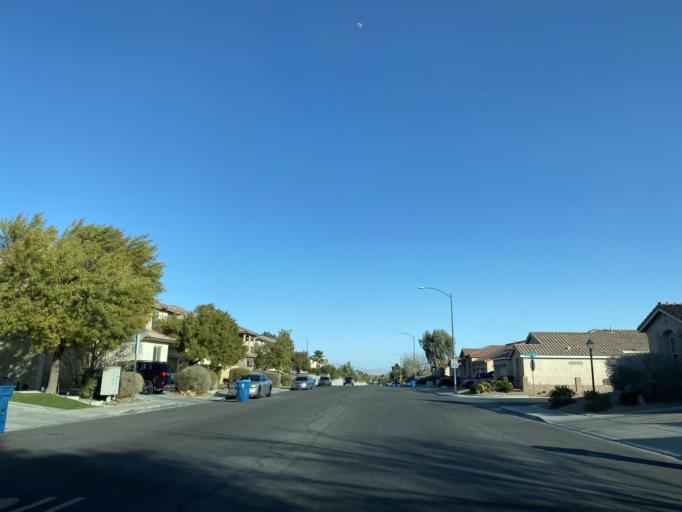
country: US
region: Nevada
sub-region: Clark County
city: Las Vegas
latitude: 36.3046
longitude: -115.2775
